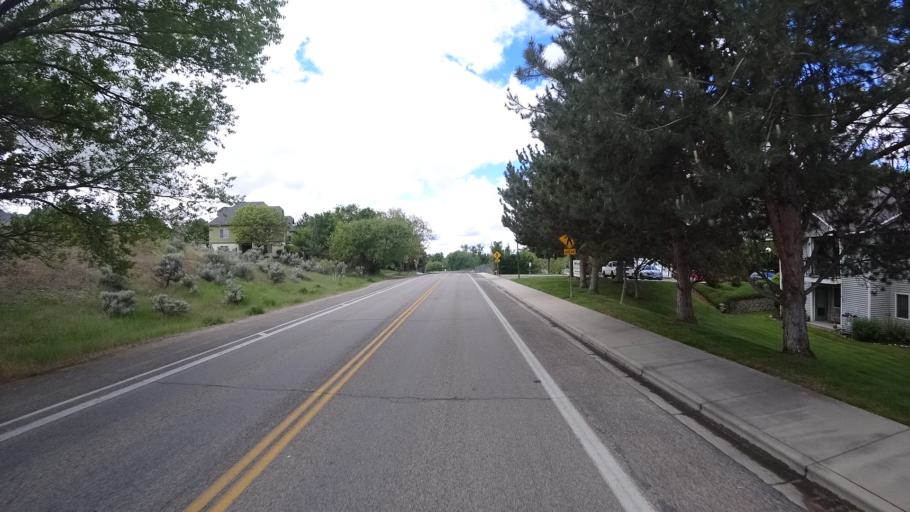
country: US
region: Idaho
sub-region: Ada County
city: Boise
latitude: 43.6412
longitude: -116.2056
